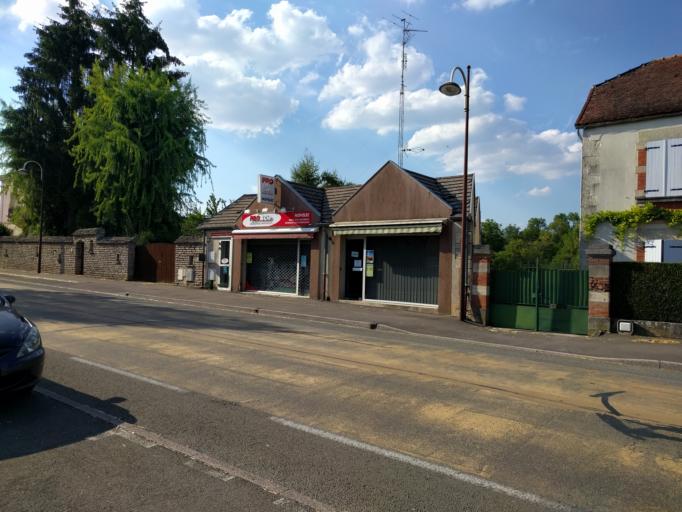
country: FR
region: Bourgogne
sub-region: Departement de la Cote-d'Or
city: Is-sur-Tille
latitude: 47.5222
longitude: 5.1178
